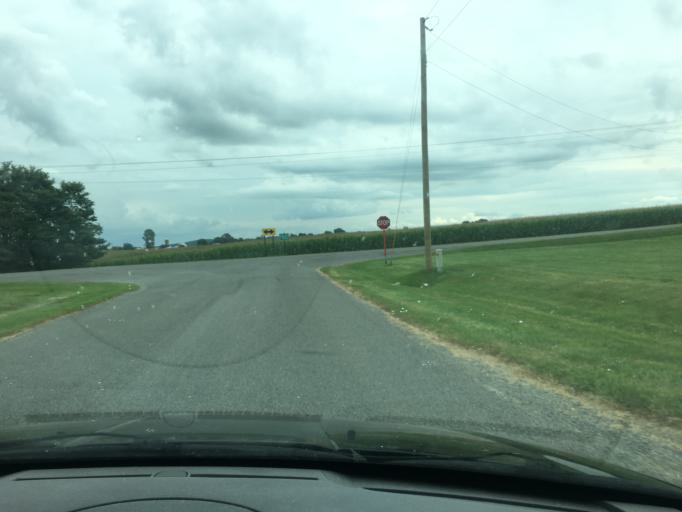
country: US
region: Ohio
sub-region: Logan County
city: West Liberty
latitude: 40.2039
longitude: -83.7109
